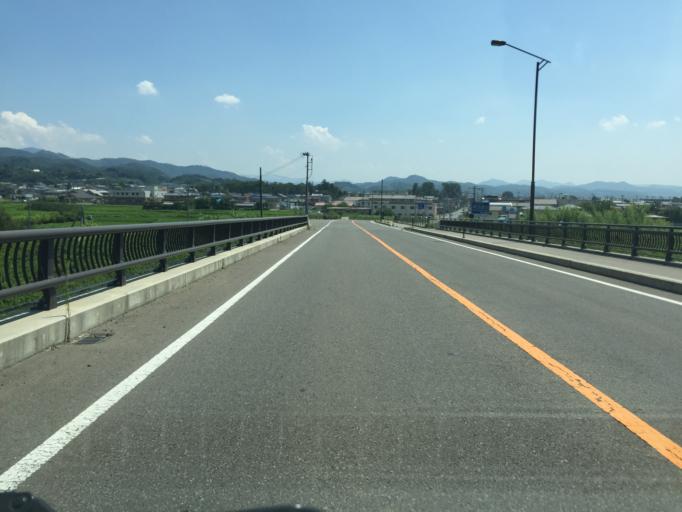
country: JP
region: Fukushima
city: Yanagawamachi-saiwaicho
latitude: 37.8679
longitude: 140.6087
